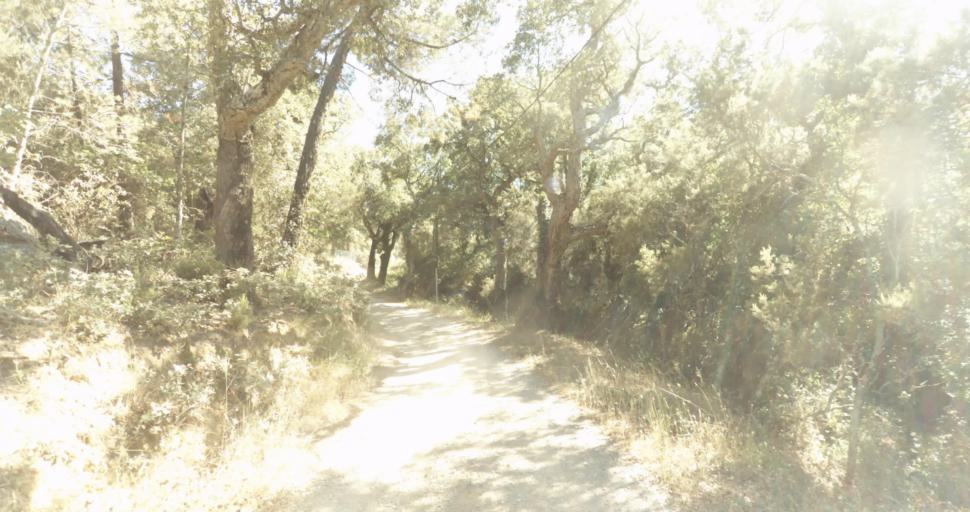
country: FR
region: Provence-Alpes-Cote d'Azur
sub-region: Departement du Var
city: Gassin
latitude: 43.2385
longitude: 6.5847
